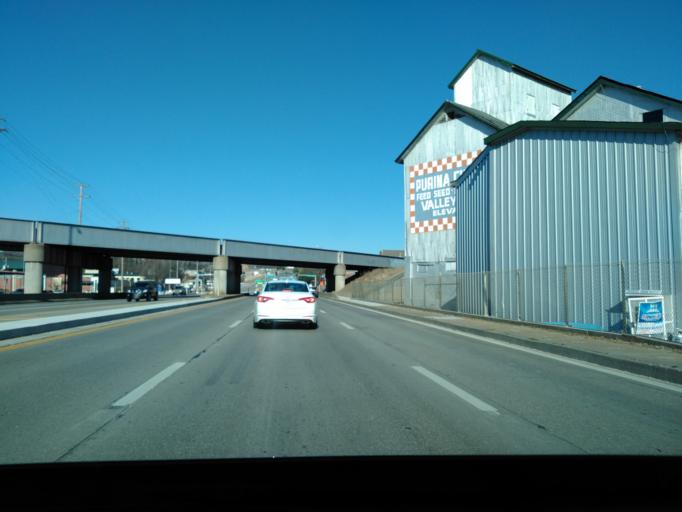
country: US
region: Missouri
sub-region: Saint Louis County
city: Valley Park
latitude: 38.5492
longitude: -90.4939
